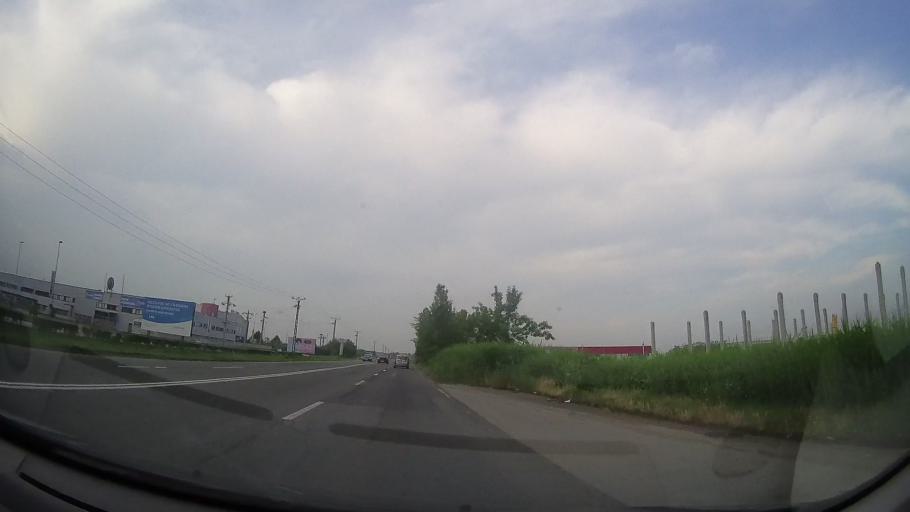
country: RO
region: Timis
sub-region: Comuna Giroc
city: Chisoda
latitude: 45.6984
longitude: 21.1803
